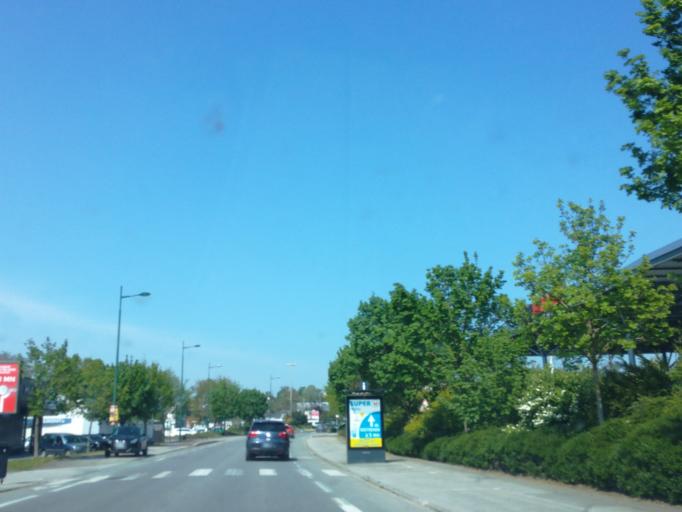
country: FR
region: Brittany
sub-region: Departement du Morbihan
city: Pontivy
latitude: 48.0519
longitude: -2.9593
